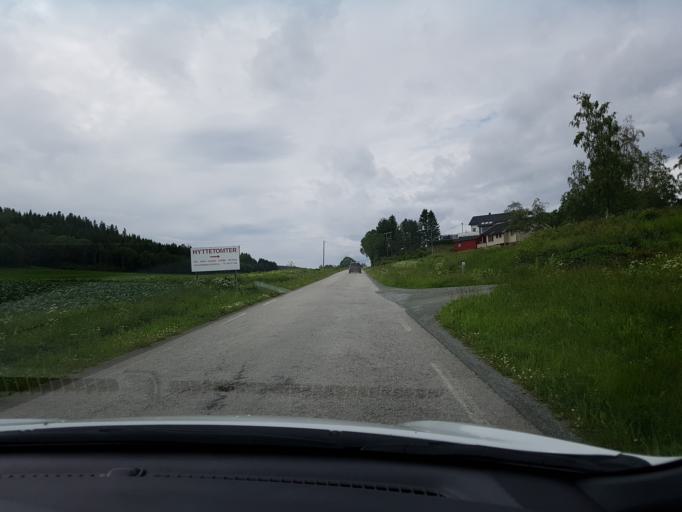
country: NO
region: Nord-Trondelag
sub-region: Frosta
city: Frosta
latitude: 63.6314
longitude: 10.7787
